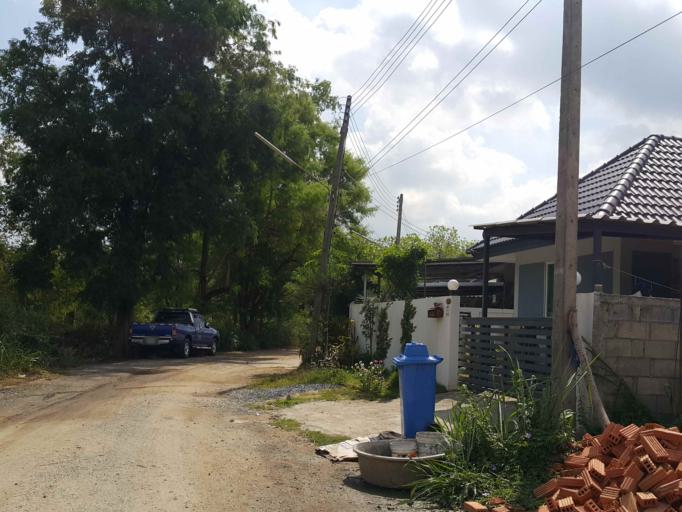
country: TH
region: Chiang Mai
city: San Kamphaeng
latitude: 18.7668
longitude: 99.0687
